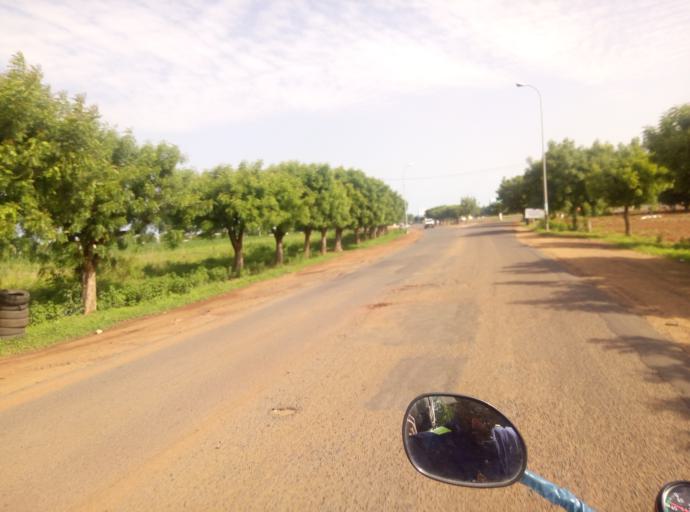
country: ML
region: Bamako
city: Bamako
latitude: 12.5480
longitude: -7.9516
